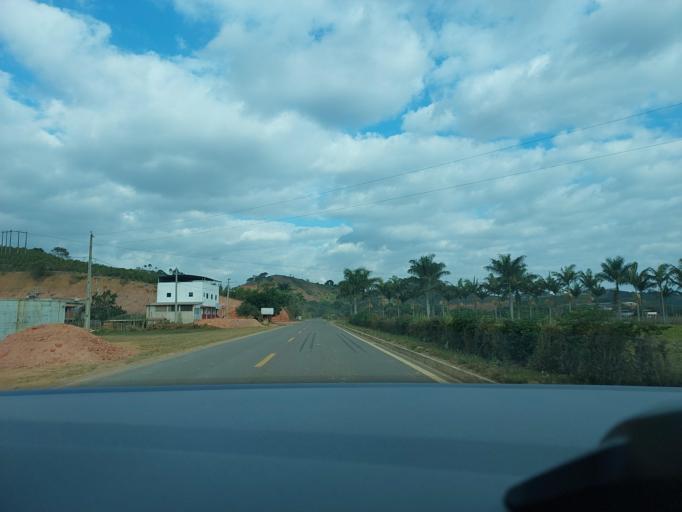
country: BR
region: Minas Gerais
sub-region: Visconde Do Rio Branco
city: Visconde do Rio Branco
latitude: -20.8927
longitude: -42.6566
